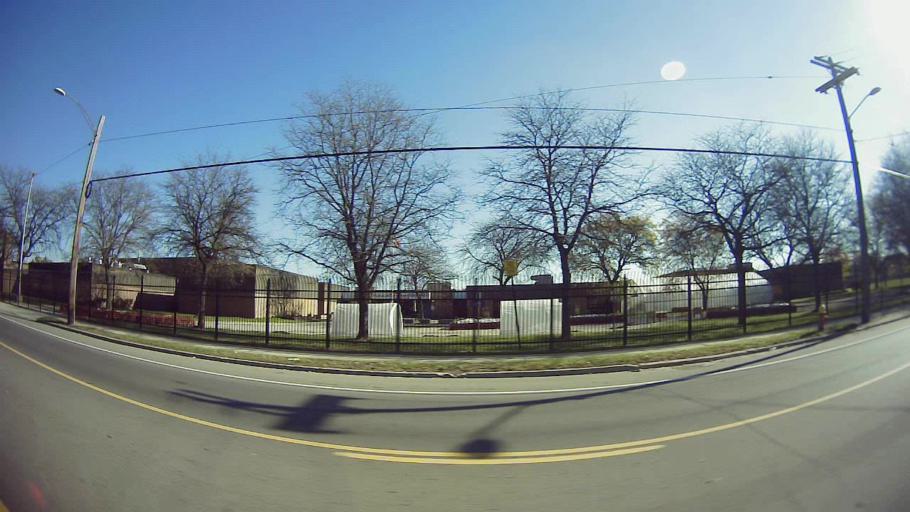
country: US
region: Michigan
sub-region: Wayne County
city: Dearborn
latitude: 42.3671
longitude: -83.1583
